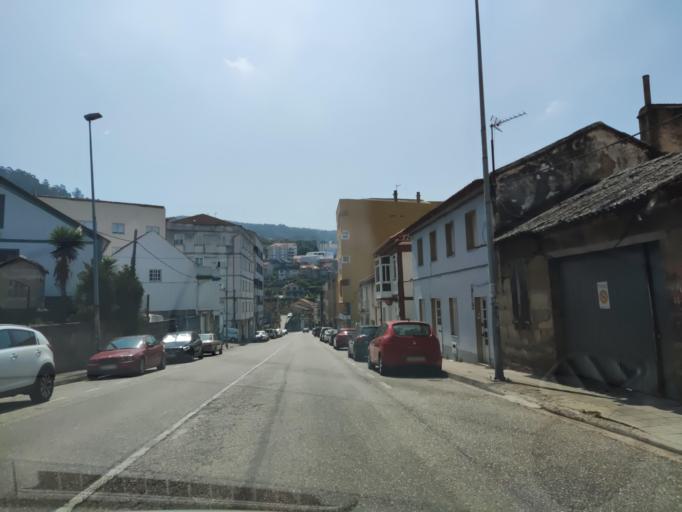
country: ES
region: Galicia
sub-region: Provincia de Pontevedra
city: Redondela
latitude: 42.2726
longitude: -8.6667
